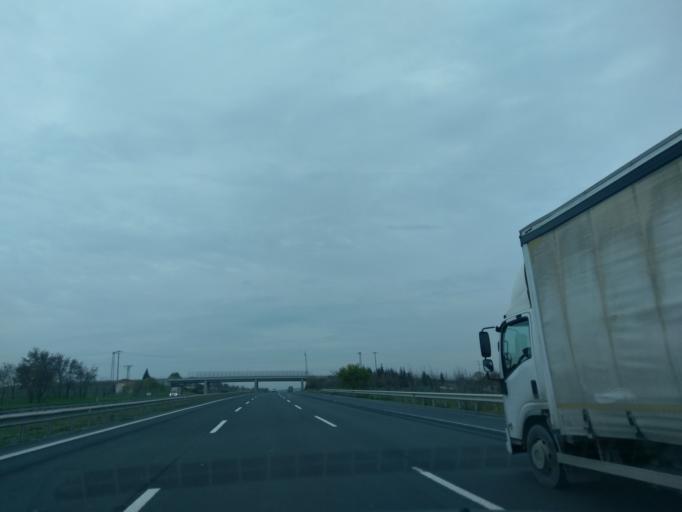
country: TR
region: Istanbul
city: Canta
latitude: 41.1387
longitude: 28.1510
